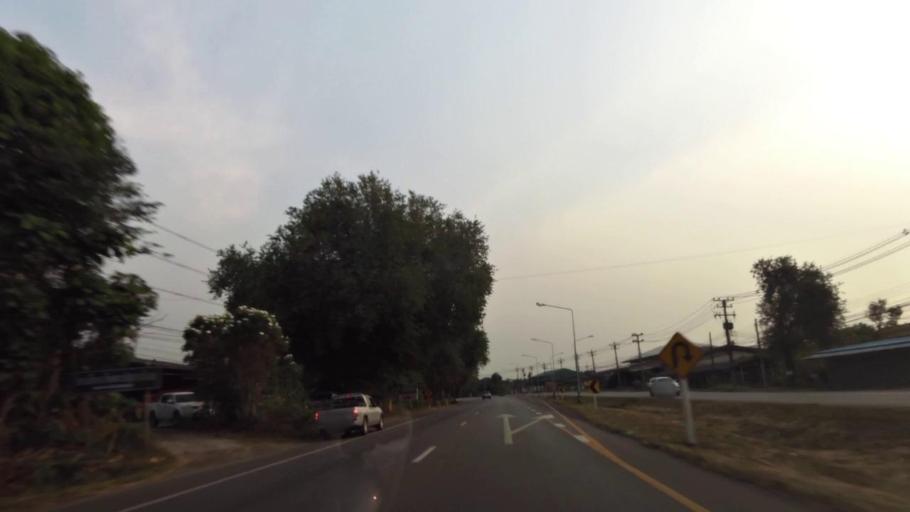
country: TH
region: Chanthaburi
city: Khlung
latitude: 12.4894
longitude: 102.1744
